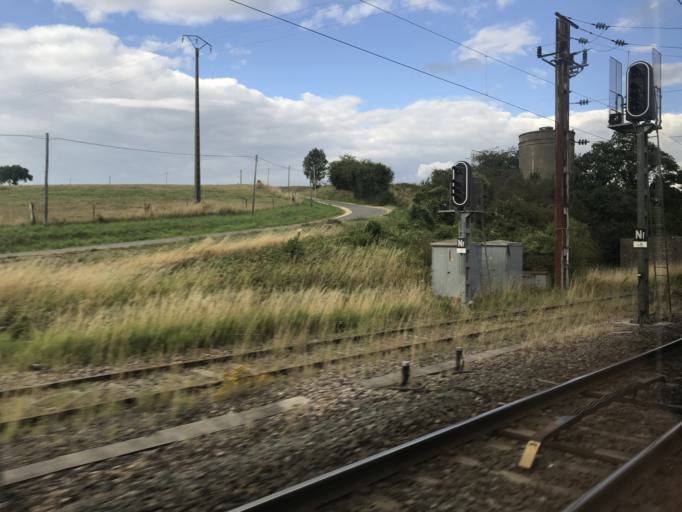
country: FR
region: Lorraine
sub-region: Departement de la Meuse
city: Montmedy
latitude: 49.5232
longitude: 5.3827
